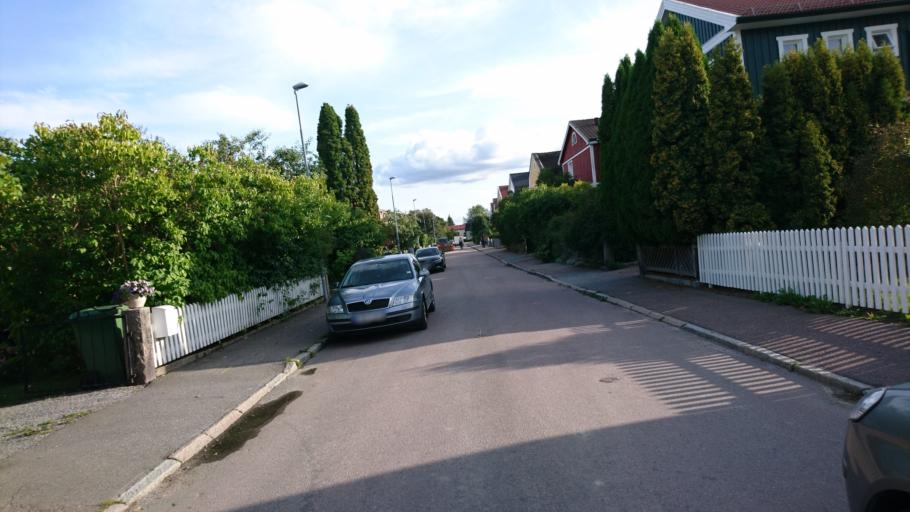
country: SE
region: Uppsala
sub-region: Uppsala Kommun
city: Uppsala
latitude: 59.8756
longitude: 17.6344
